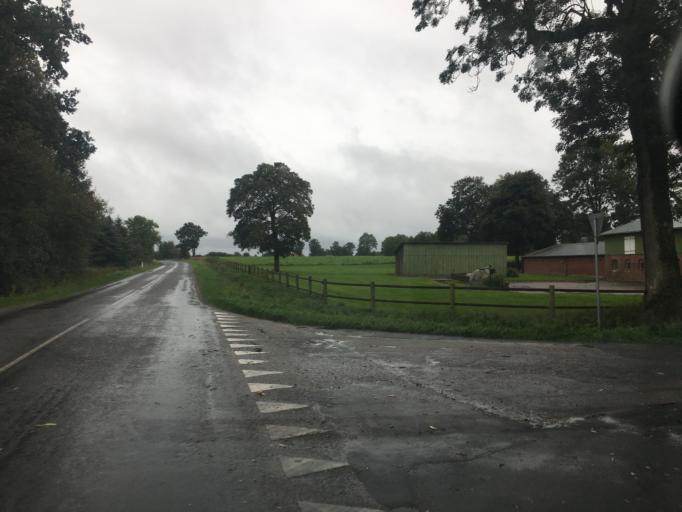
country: DE
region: Schleswig-Holstein
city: Bramstedtlund
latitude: 54.9577
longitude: 9.0534
